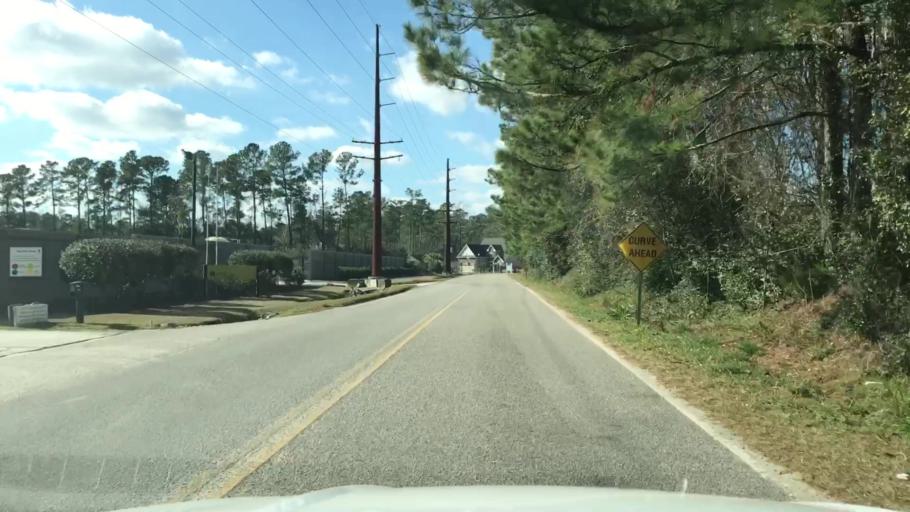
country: US
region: South Carolina
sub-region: Horry County
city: Socastee
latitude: 33.6587
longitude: -78.9969
